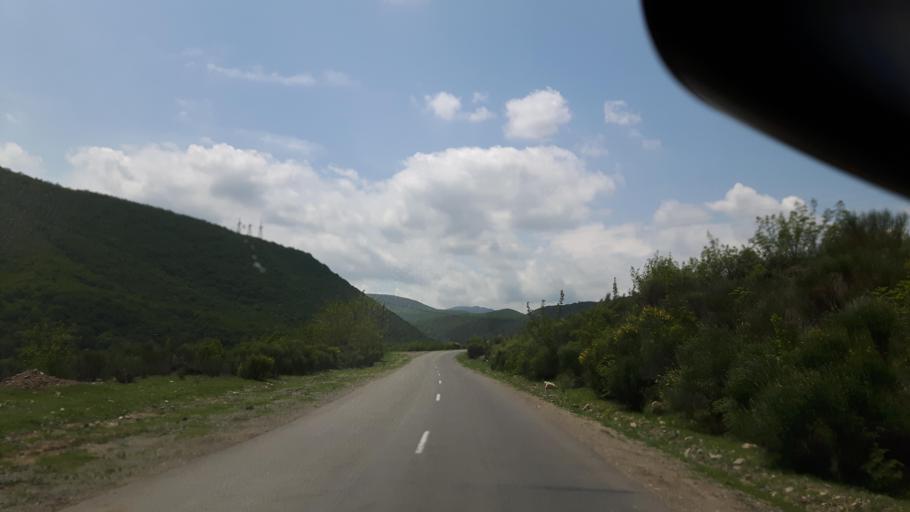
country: GE
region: Mtskheta-Mtianeti
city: Mtskheta
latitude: 41.8394
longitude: 44.5825
